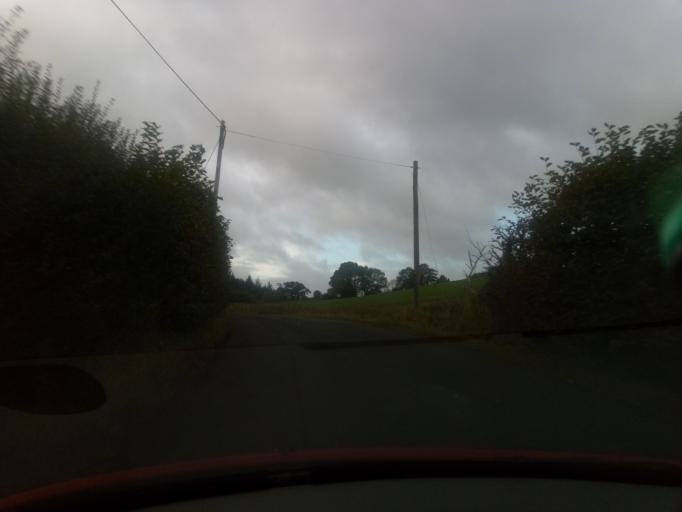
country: GB
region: Scotland
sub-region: The Scottish Borders
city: Jedburgh
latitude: 55.4548
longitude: -2.5587
